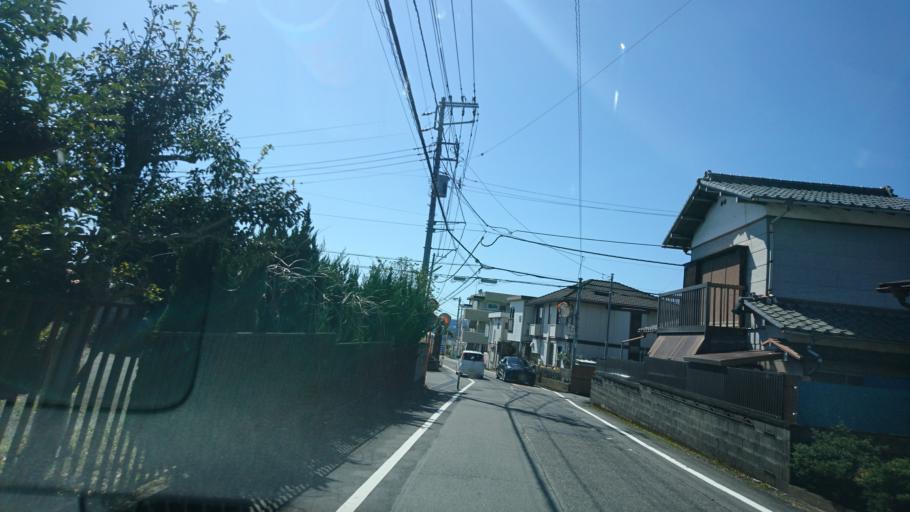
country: JP
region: Shizuoka
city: Fujinomiya
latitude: 35.2472
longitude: 138.6114
